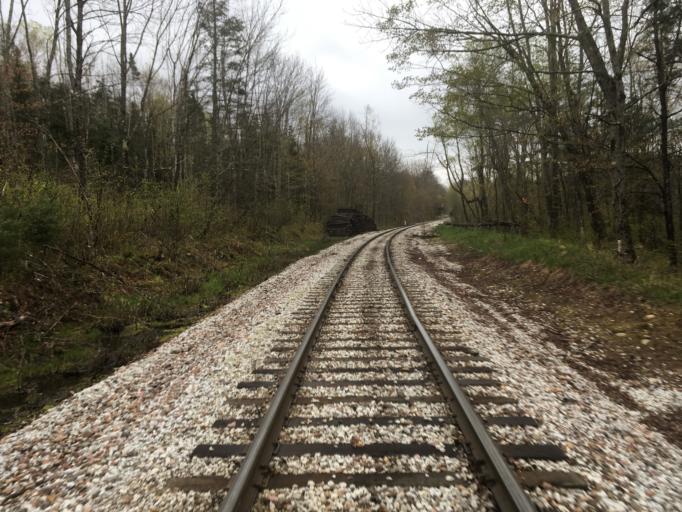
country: US
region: Vermont
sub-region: Rutland County
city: Rutland
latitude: 43.4726
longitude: -72.8716
